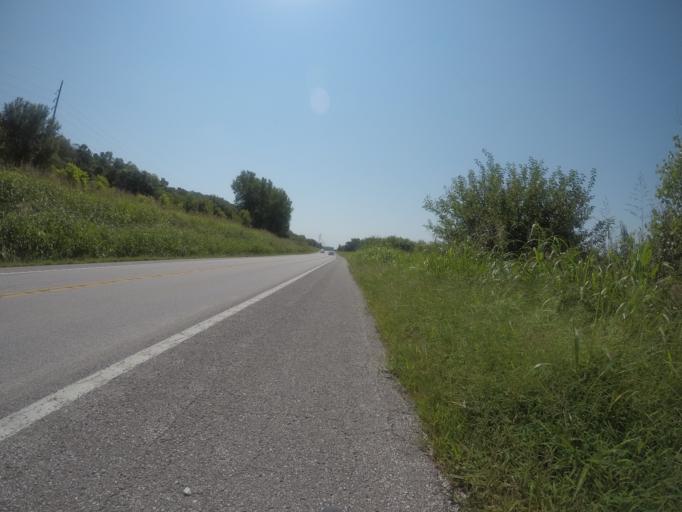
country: US
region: Kansas
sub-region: Atchison County
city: Atchison
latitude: 39.5445
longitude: -95.0439
